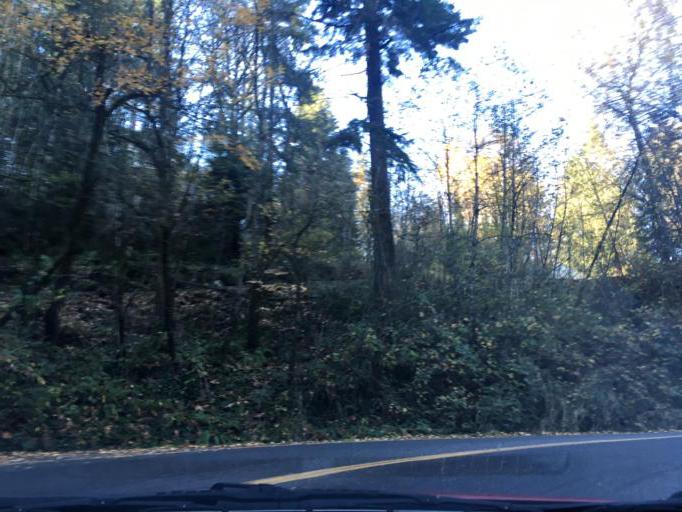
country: US
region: Oregon
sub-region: Washington County
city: Cedar Mill
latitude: 45.5893
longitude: -122.7823
